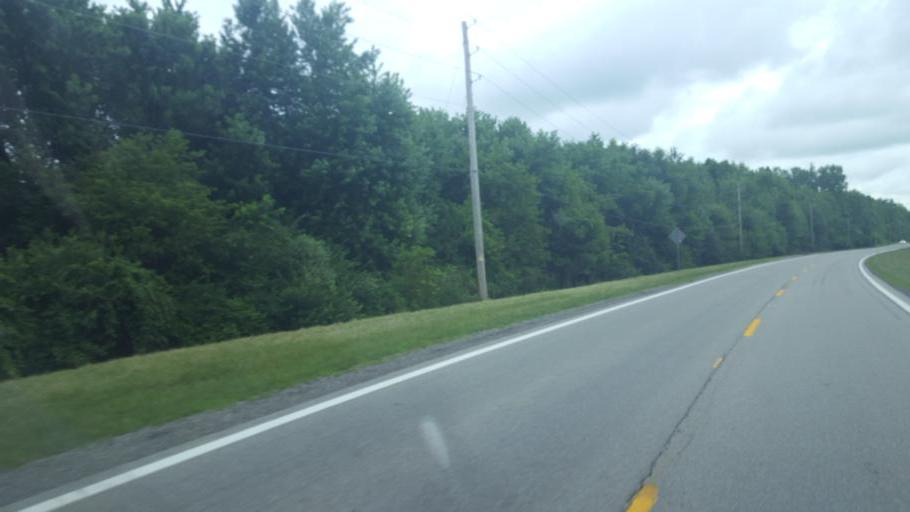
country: US
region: Ohio
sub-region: Pickaway County
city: Commercial Point
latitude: 39.7739
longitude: -83.0008
